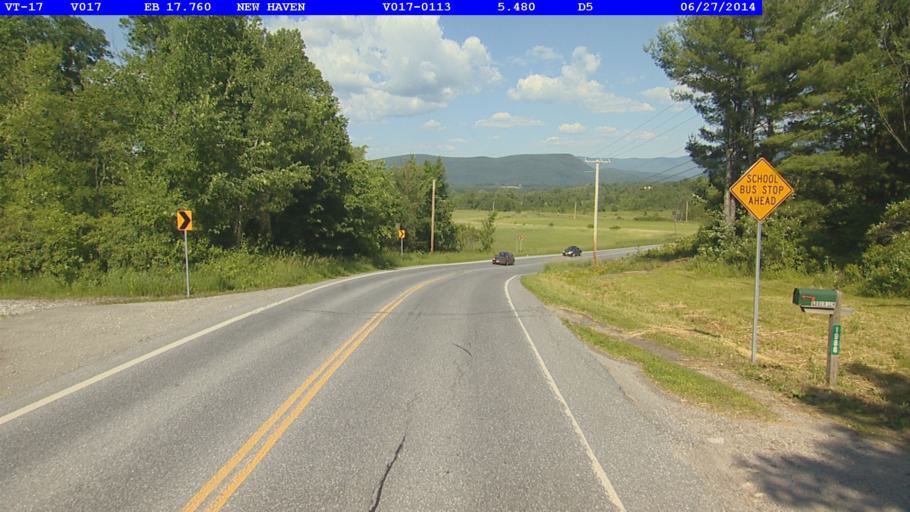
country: US
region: Vermont
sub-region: Addison County
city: Bristol
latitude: 44.1253
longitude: -73.1414
